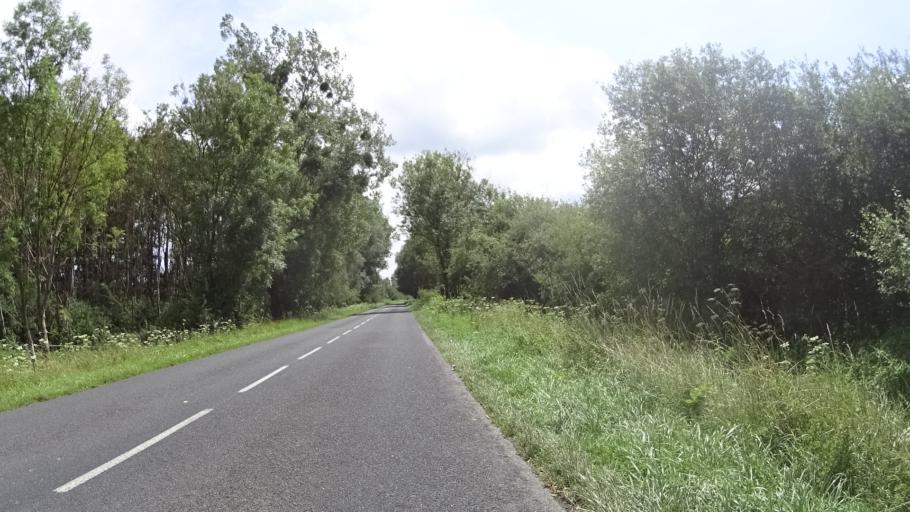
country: FR
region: Lorraine
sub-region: Departement de la Meuse
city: Euville
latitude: 48.7249
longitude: 5.6646
